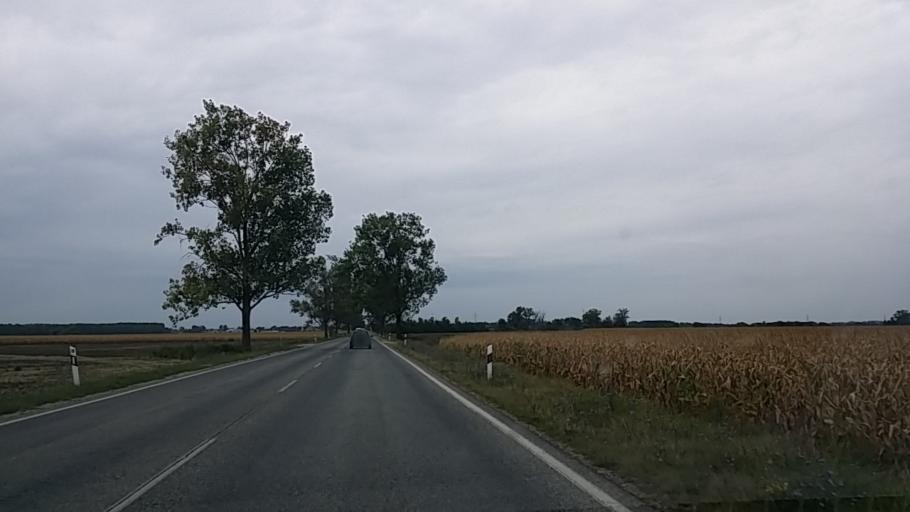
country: HU
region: Gyor-Moson-Sopron
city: Kapuvar
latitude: 47.5892
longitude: 17.0741
